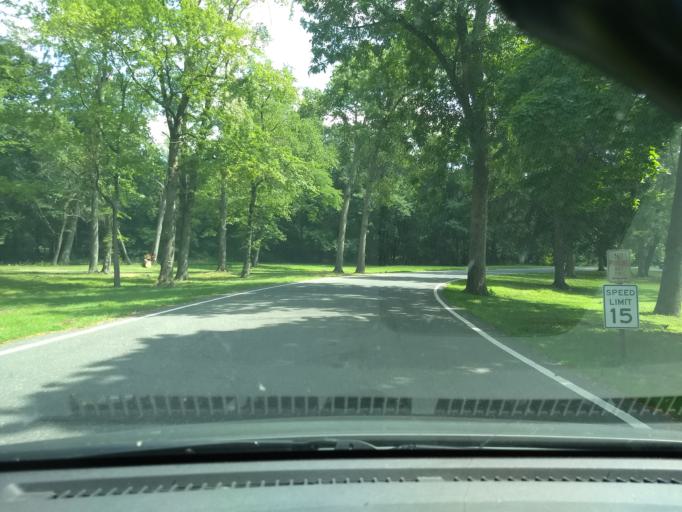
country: US
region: New Jersey
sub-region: Bergen County
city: Ho-Ho-Kus
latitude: 40.9765
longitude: -74.0931
